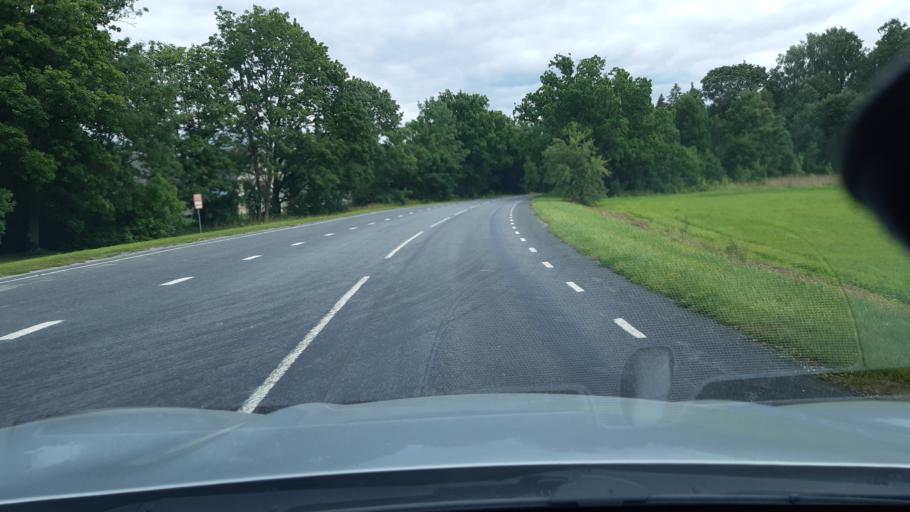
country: EE
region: Raplamaa
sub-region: Maerjamaa vald
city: Marjamaa
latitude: 59.0455
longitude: 24.5294
